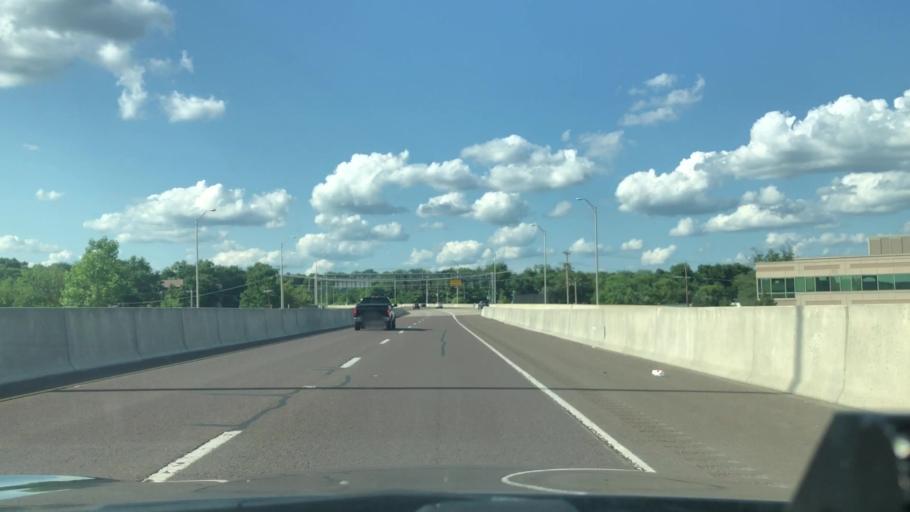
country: US
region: Pennsylvania
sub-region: Montgomery County
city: Fort Washington
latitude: 40.1356
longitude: -75.2013
